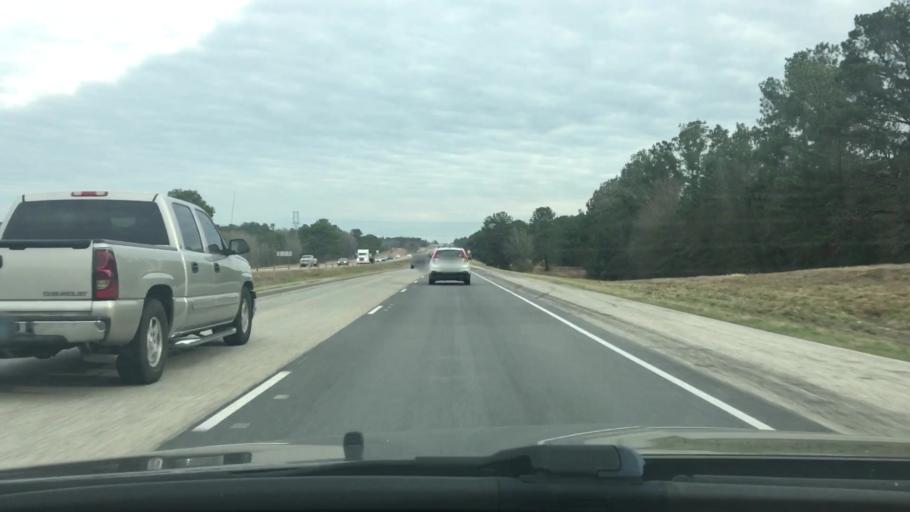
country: US
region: Texas
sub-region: Walker County
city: Huntsville
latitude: 30.7932
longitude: -95.6759
